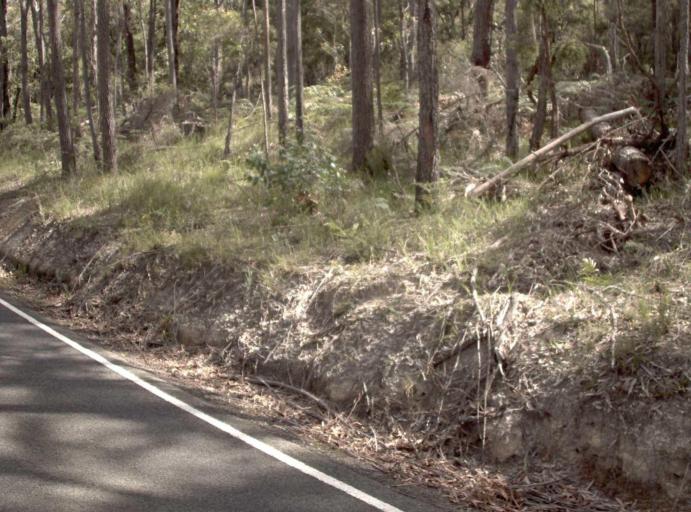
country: AU
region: New South Wales
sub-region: Bega Valley
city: Eden
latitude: -37.5407
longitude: 149.6970
